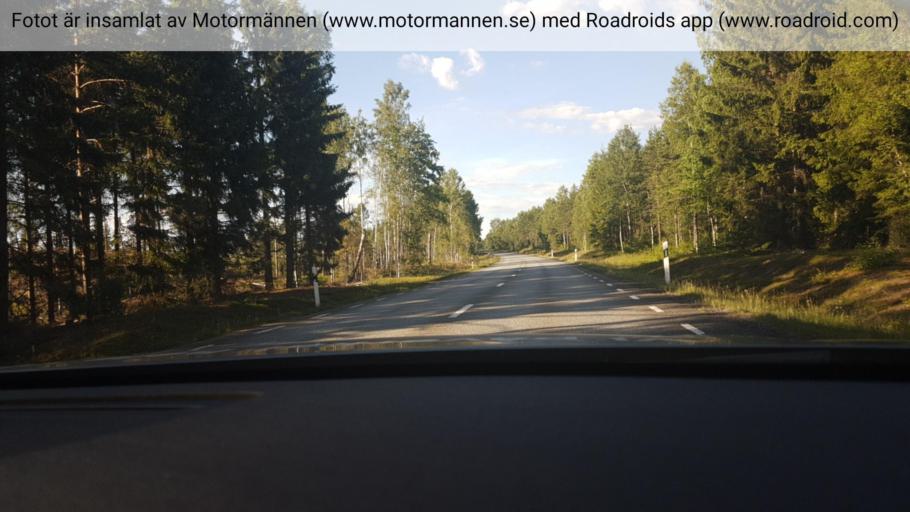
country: SE
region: Joenkoeping
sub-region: Jonkopings Kommun
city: Taberg
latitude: 57.6639
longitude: 13.8372
